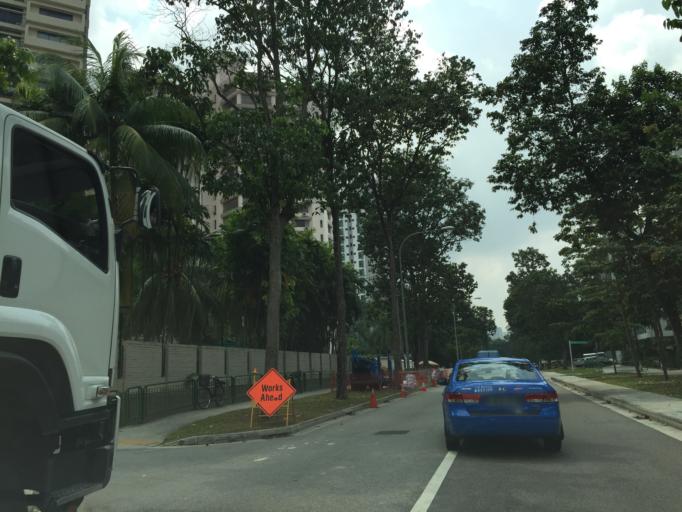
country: SG
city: Singapore
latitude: 1.3157
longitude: 103.8332
